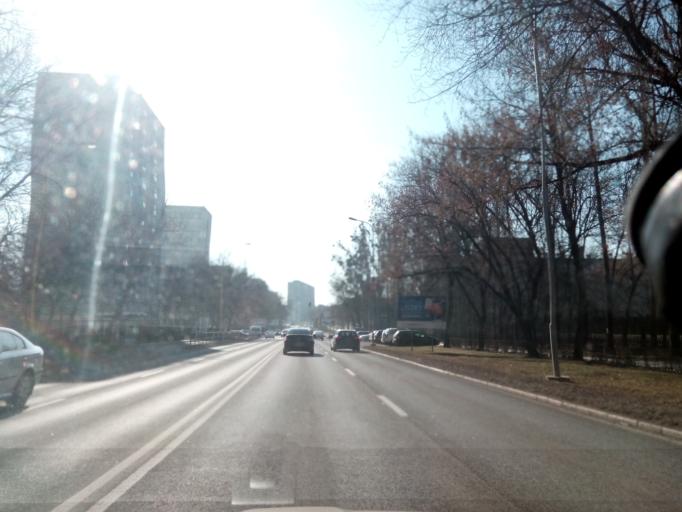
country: SK
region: Kosicky
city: Kosice
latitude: 48.7318
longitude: 21.2386
